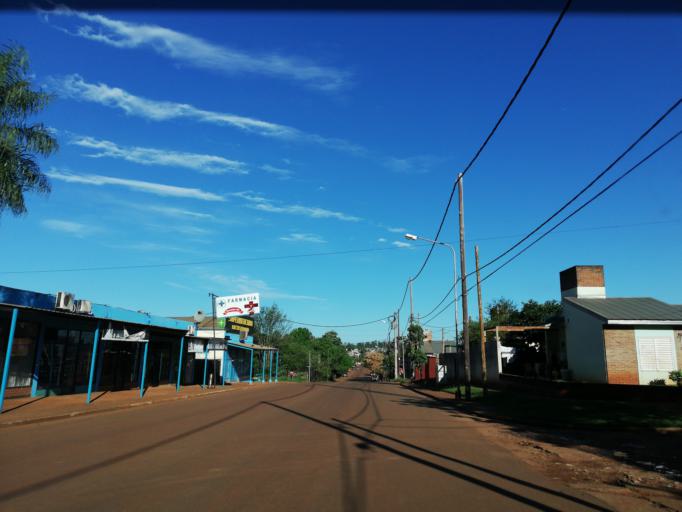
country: AR
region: Misiones
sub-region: Departamento de Capital
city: Posadas
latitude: -27.4267
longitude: -55.9562
